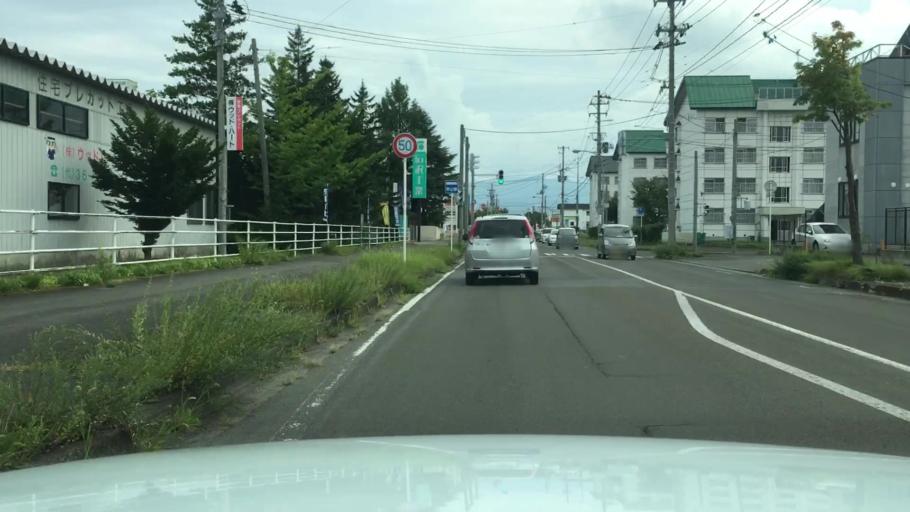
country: JP
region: Aomori
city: Hirosaki
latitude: 40.6211
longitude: 140.4848
